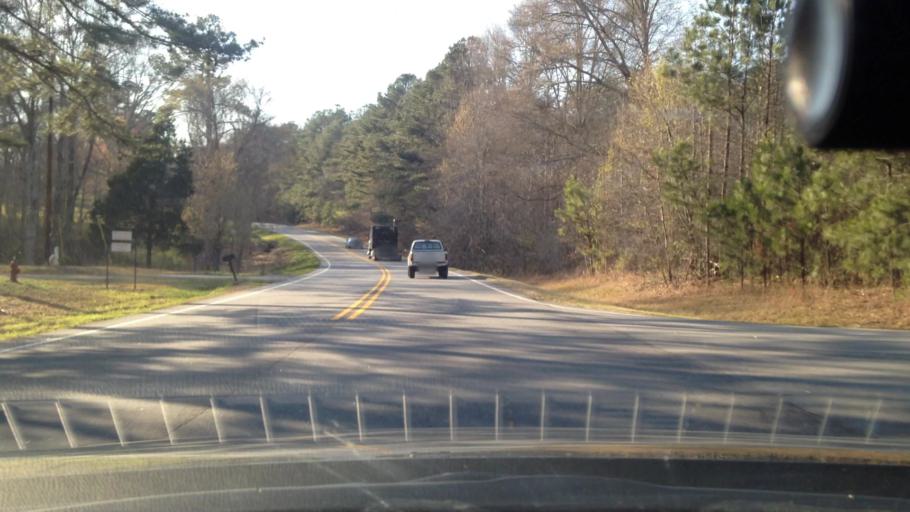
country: US
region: Georgia
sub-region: Fayette County
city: Peachtree City
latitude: 33.3386
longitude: -84.6521
